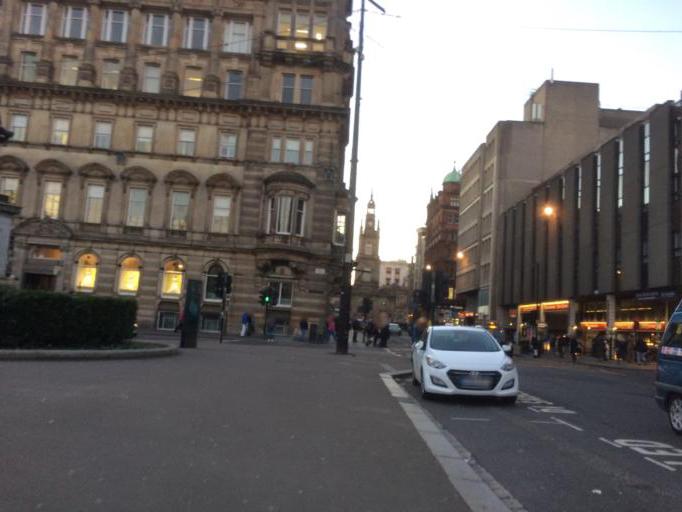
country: GB
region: Scotland
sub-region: Glasgow City
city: Glasgow
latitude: 55.8616
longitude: -4.2507
